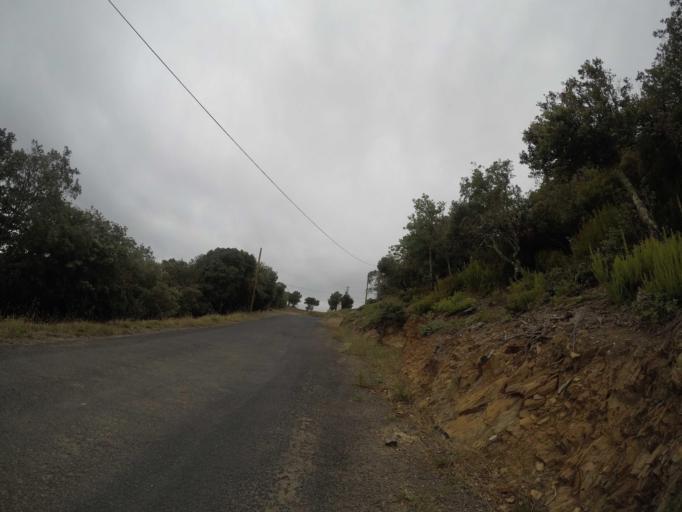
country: FR
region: Languedoc-Roussillon
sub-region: Departement des Pyrenees-Orientales
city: Ille-sur-Tet
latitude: 42.6171
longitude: 2.6198
